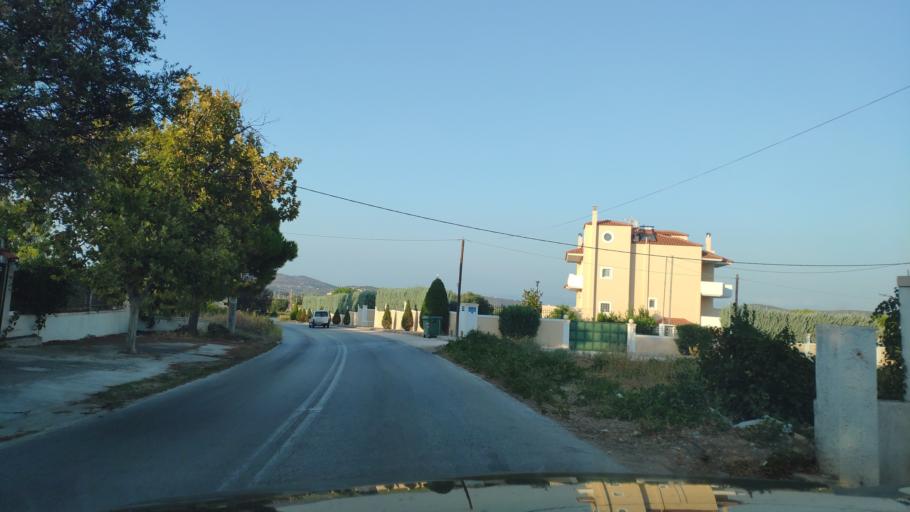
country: GR
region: Attica
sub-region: Nomarchia Anatolikis Attikis
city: Markopoulo
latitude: 37.9007
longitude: 23.9581
